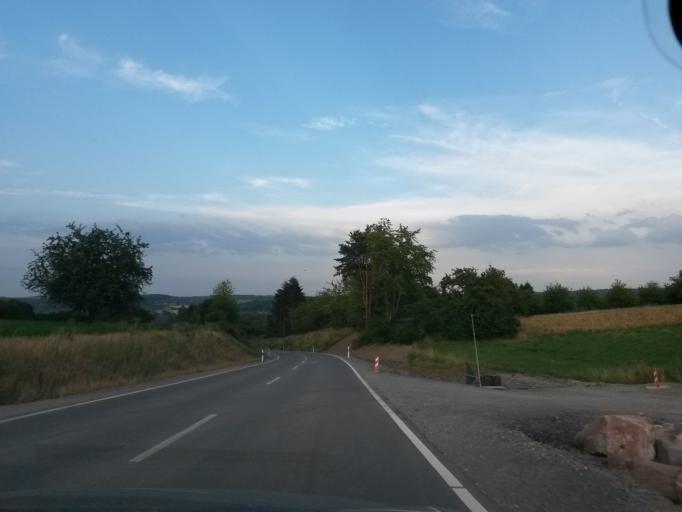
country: DE
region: Baden-Wuerttemberg
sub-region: Karlsruhe Region
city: Konigsbach-Stein
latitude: 48.9351
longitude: 8.5520
